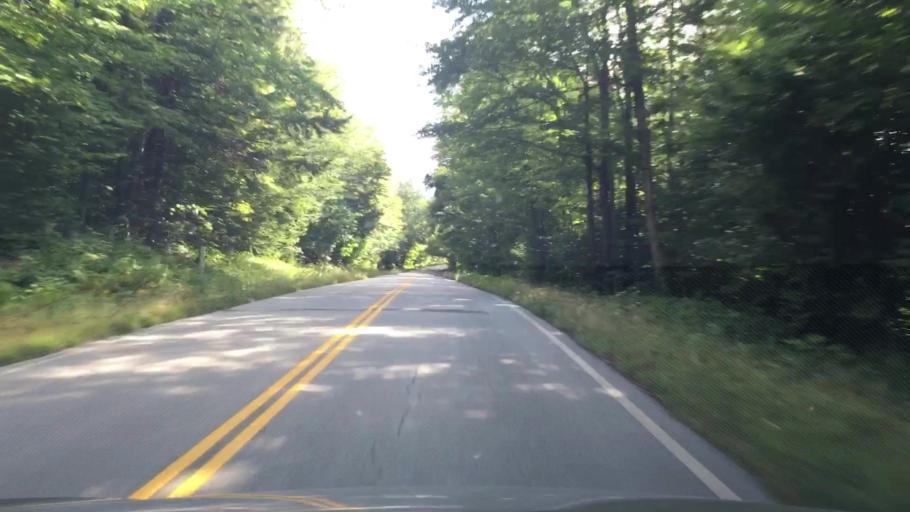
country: US
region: New Hampshire
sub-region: Carroll County
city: Tamworth
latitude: 44.0140
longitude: -71.3208
